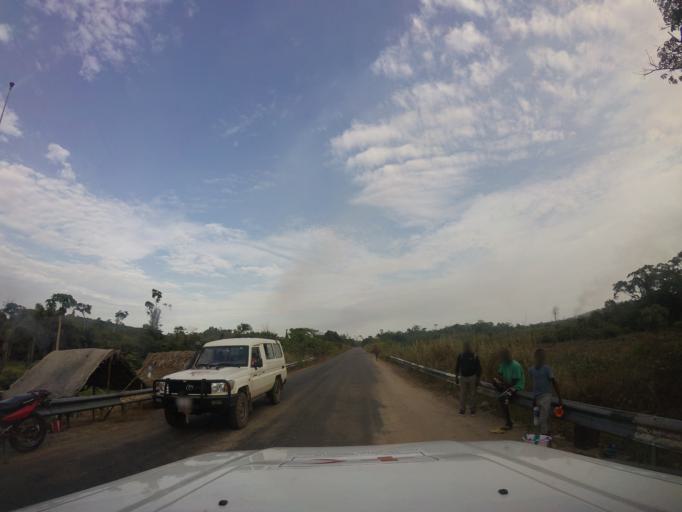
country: LR
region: Grand Cape Mount
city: Robertsport
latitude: 6.8605
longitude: -11.1906
